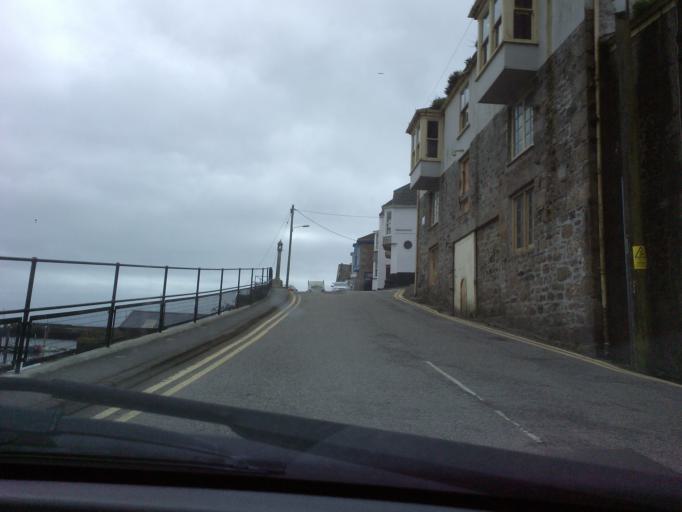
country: GB
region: England
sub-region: Cornwall
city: Penzance
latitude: 50.1031
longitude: -5.5493
